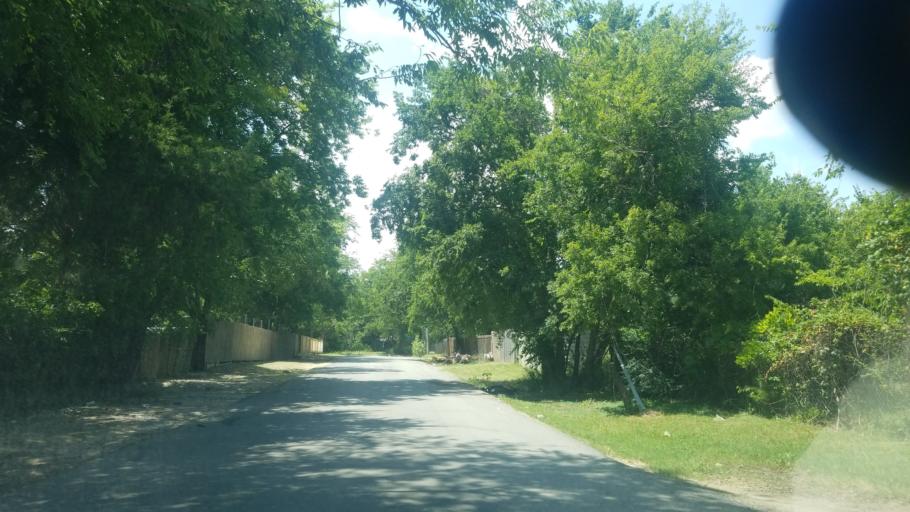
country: US
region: Texas
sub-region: Dallas County
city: Dallas
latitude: 32.7133
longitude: -96.7704
